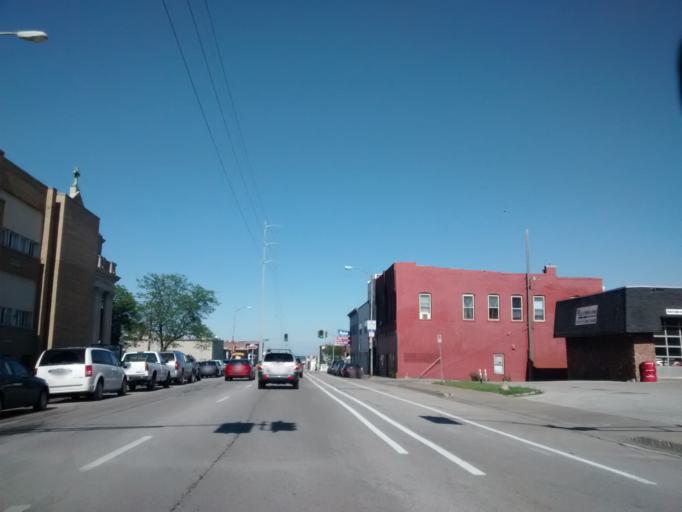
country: US
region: Nebraska
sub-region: Douglas County
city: Omaha
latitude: 41.2524
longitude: -95.9532
